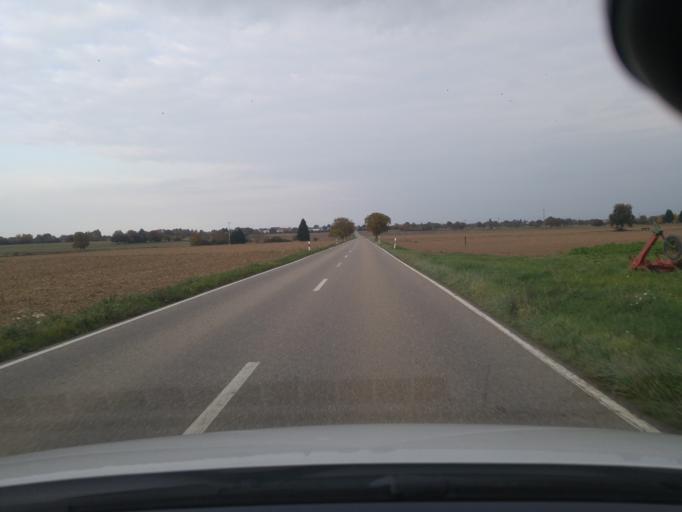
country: DE
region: Rheinland-Pfalz
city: Harthausen
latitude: 49.2720
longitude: 8.3825
